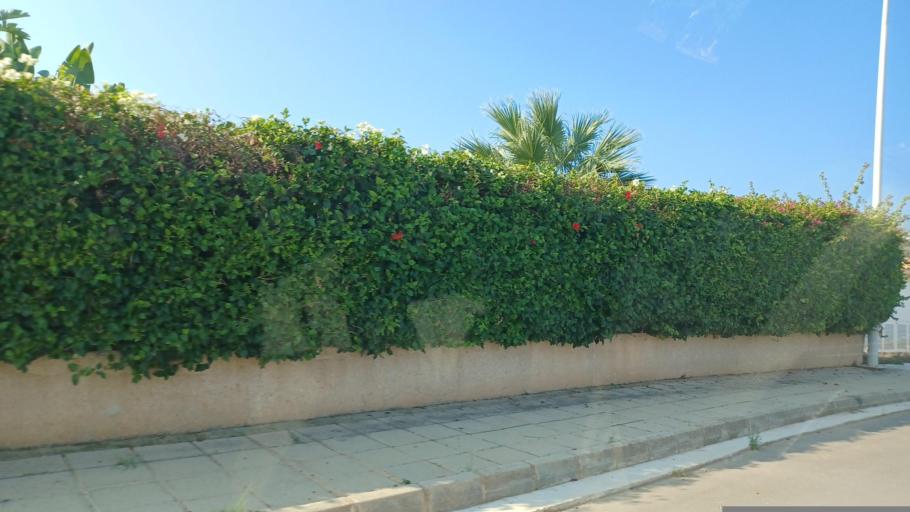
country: CY
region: Pafos
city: Pegeia
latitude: 34.8992
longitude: 32.3273
